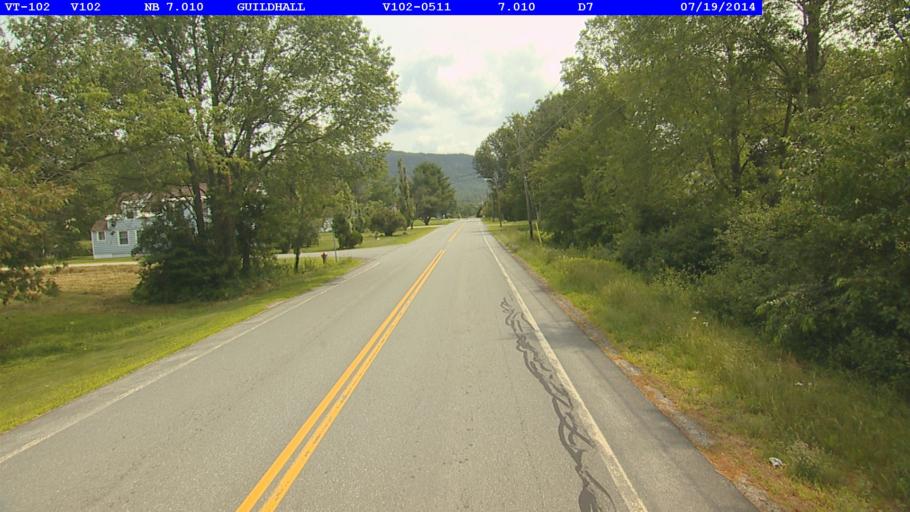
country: US
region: Vermont
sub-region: Essex County
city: Guildhall
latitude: 44.5651
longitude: -71.5656
